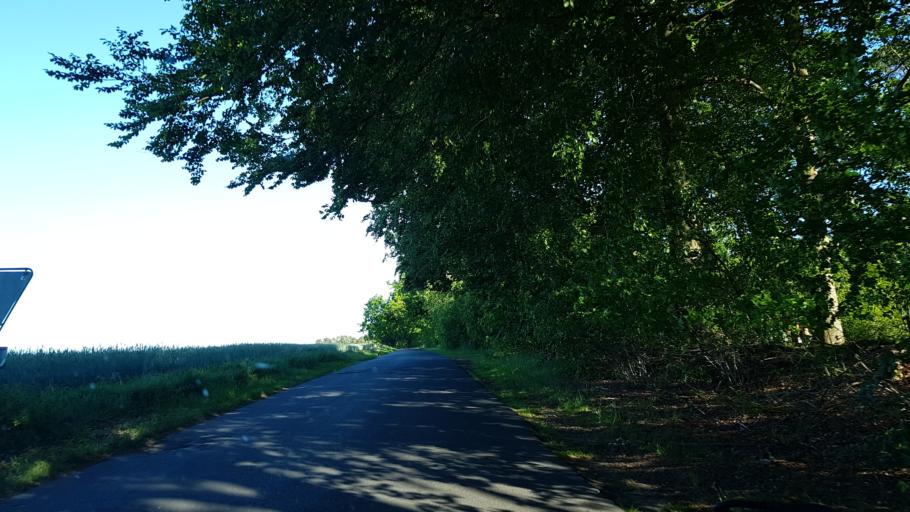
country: DE
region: Lower Saxony
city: Brackel
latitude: 53.3188
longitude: 10.0640
